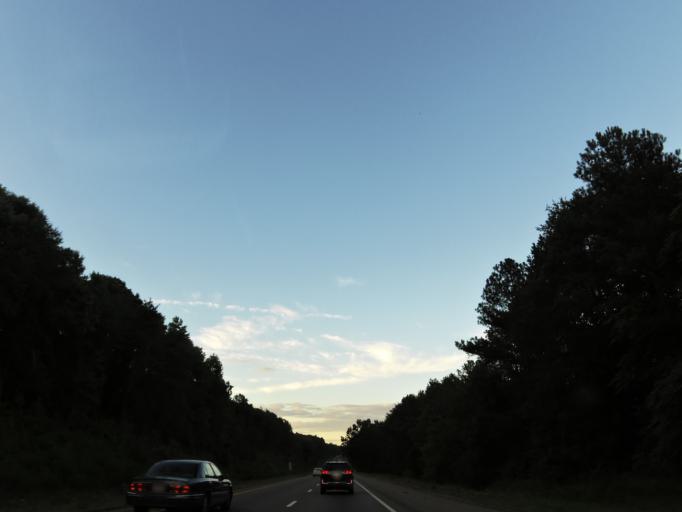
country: US
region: Tennessee
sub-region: Meigs County
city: Decatur
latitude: 35.3792
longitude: -84.7294
